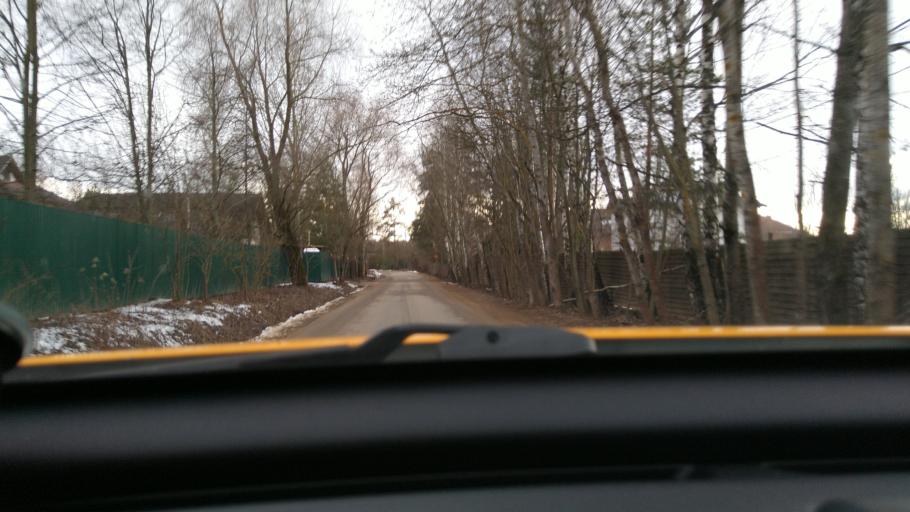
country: RU
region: Moskovskaya
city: Petrovo-Dal'neye
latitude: 55.7676
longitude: 37.2078
